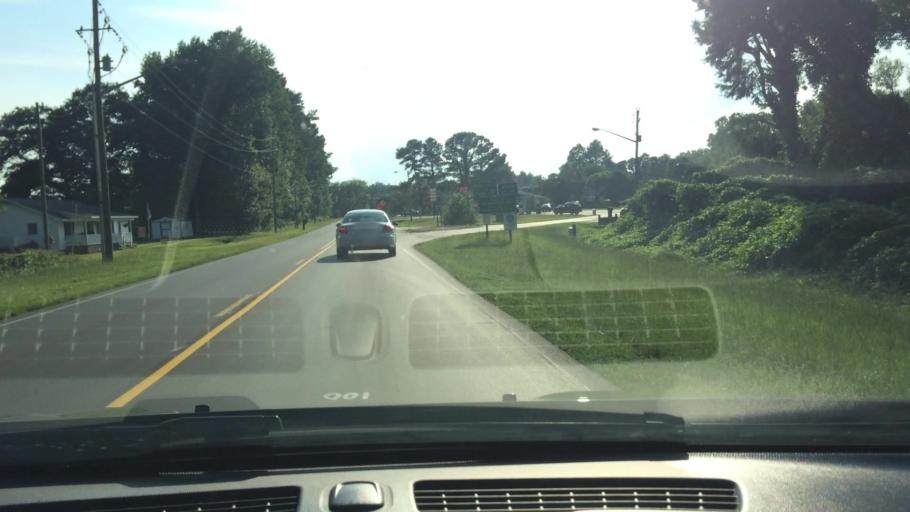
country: US
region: North Carolina
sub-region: Pitt County
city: Ayden
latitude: 35.4711
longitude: -77.4022
